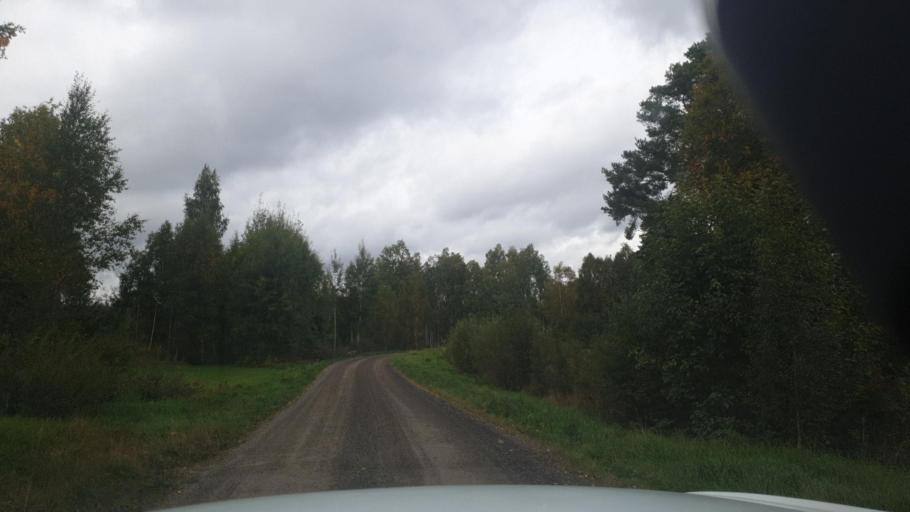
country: SE
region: Vaermland
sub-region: Torsby Kommun
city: Torsby
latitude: 59.9357
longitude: 12.8174
